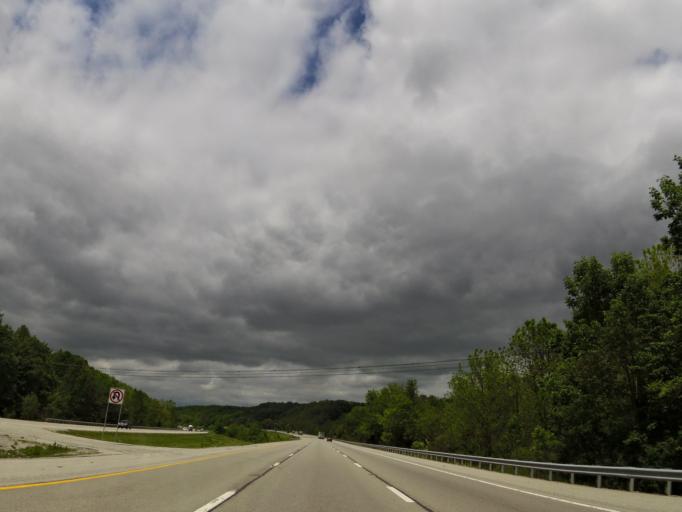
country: US
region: Kentucky
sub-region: Madison County
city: Berea
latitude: 37.5158
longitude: -84.3203
